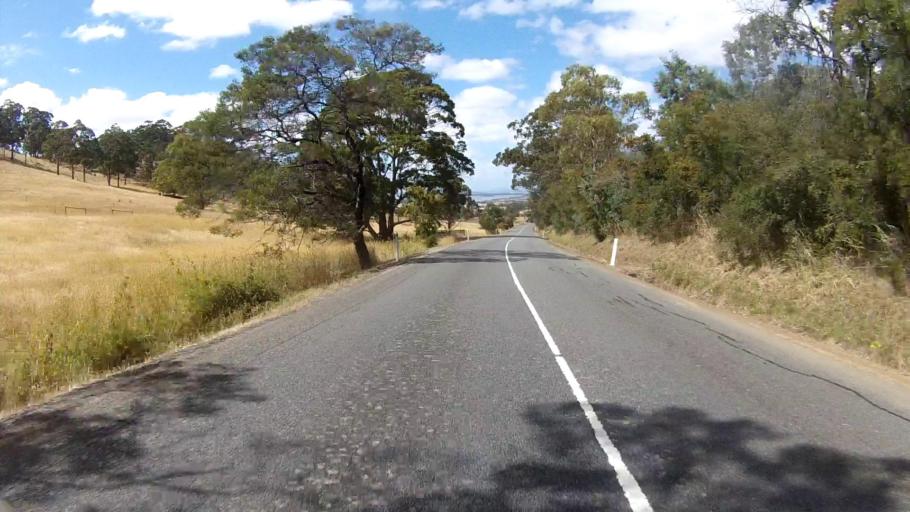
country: AU
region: Tasmania
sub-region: Sorell
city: Sorell
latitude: -42.7365
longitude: 147.4811
